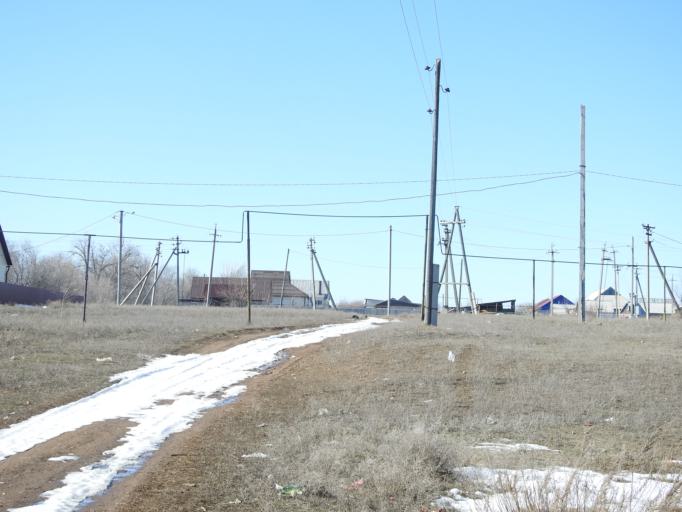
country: RU
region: Saratov
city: Yershov
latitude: 51.3703
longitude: 48.2365
